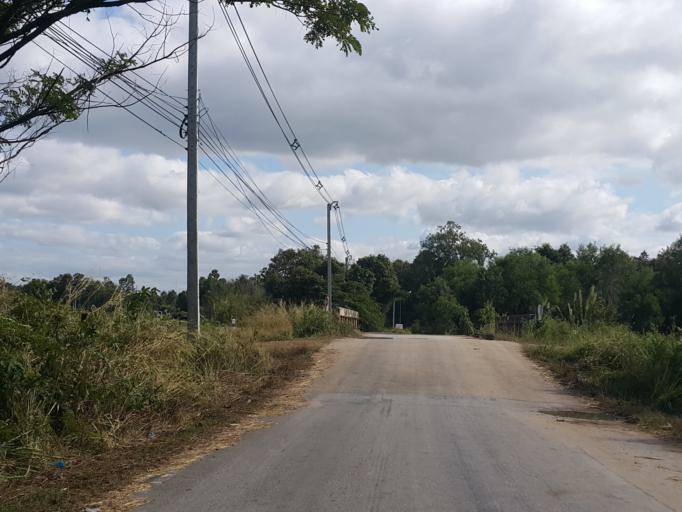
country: TH
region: Lampang
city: Hang Chat
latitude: 18.3288
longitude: 99.3889
